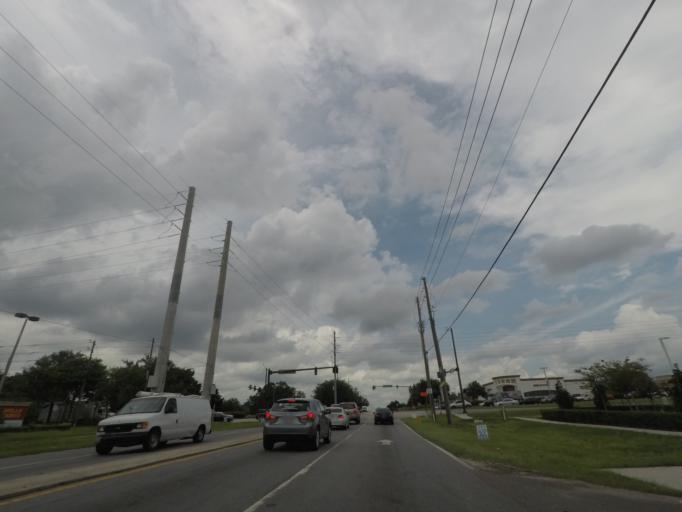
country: US
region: Florida
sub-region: Polk County
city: Loughman
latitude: 28.2590
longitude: -81.5906
